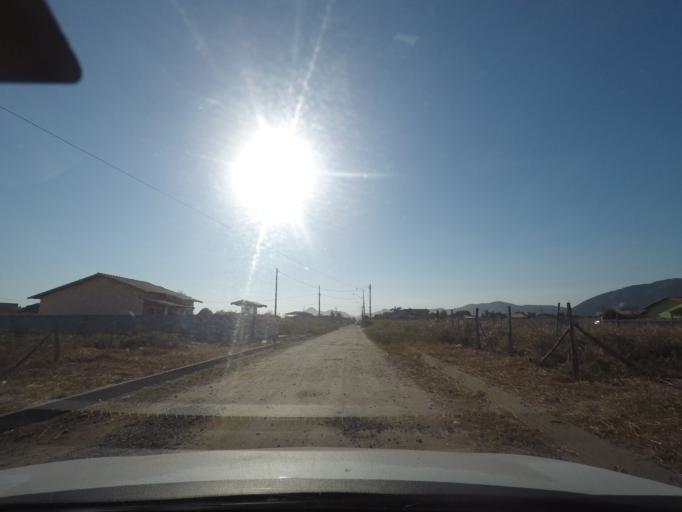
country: BR
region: Rio de Janeiro
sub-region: Marica
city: Marica
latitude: -22.9619
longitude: -42.9318
